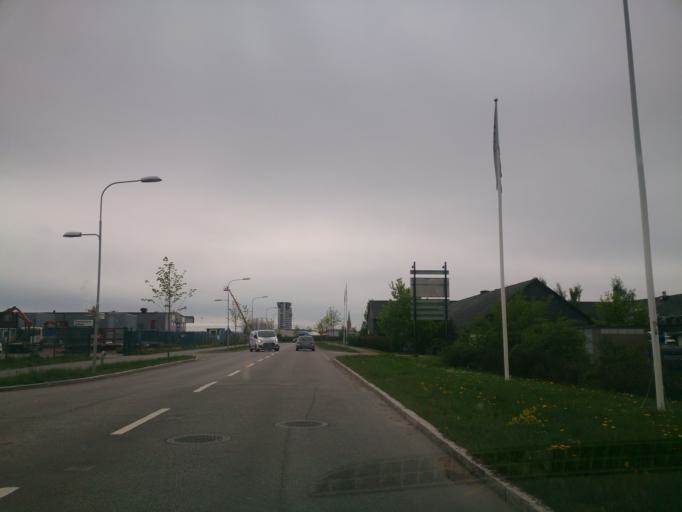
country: SE
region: OEstergoetland
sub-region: Linkopings Kommun
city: Linkoping
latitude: 58.4307
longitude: 15.6125
